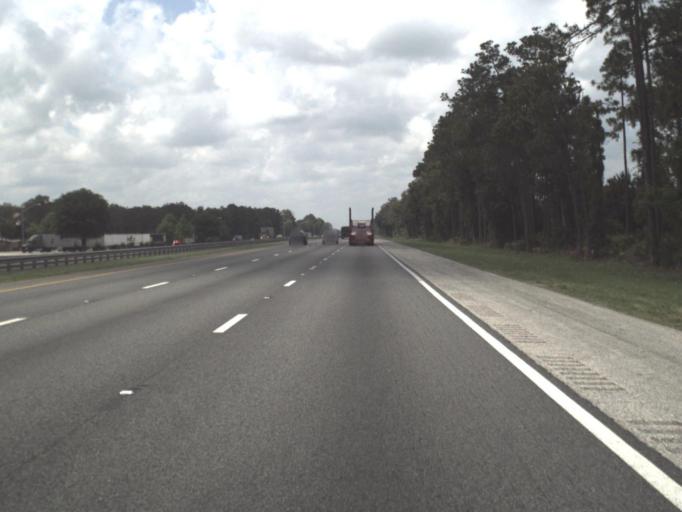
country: US
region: Florida
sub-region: Saint Johns County
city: Saint Augustine Shores
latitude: 29.7135
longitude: -81.3326
